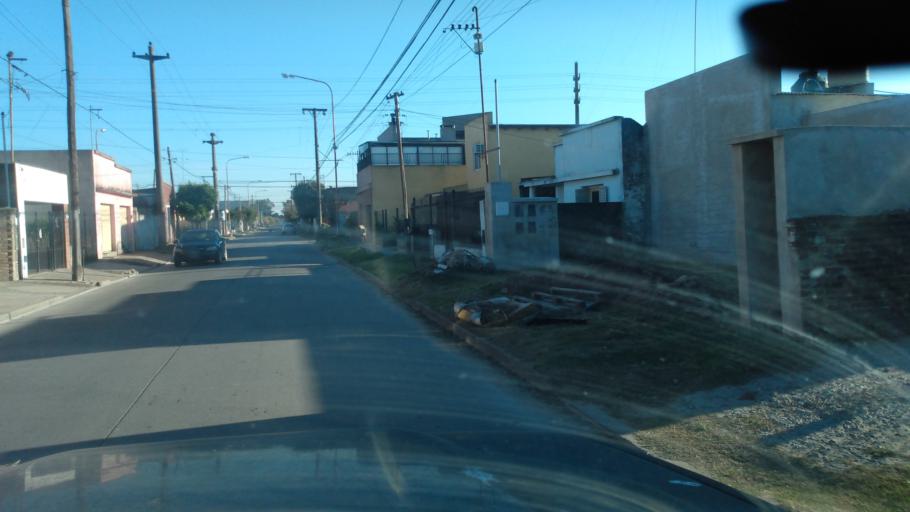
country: AR
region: Buenos Aires
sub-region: Partido de Lujan
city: Lujan
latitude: -34.5660
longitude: -59.0934
